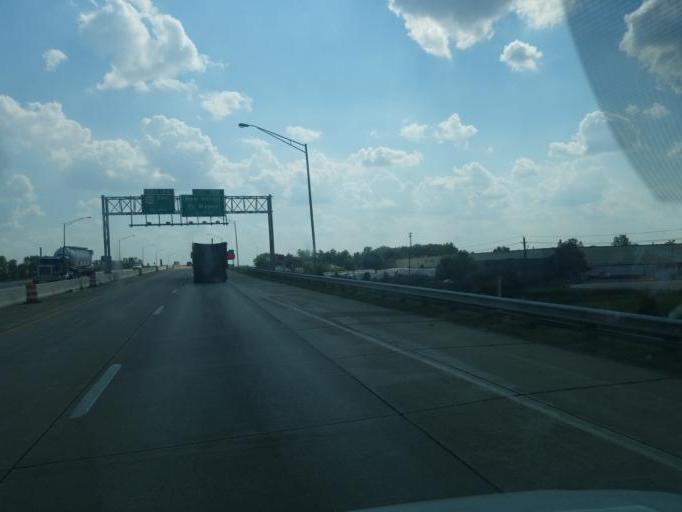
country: US
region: Indiana
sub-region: Allen County
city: New Haven
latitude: 41.0755
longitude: -84.9909
